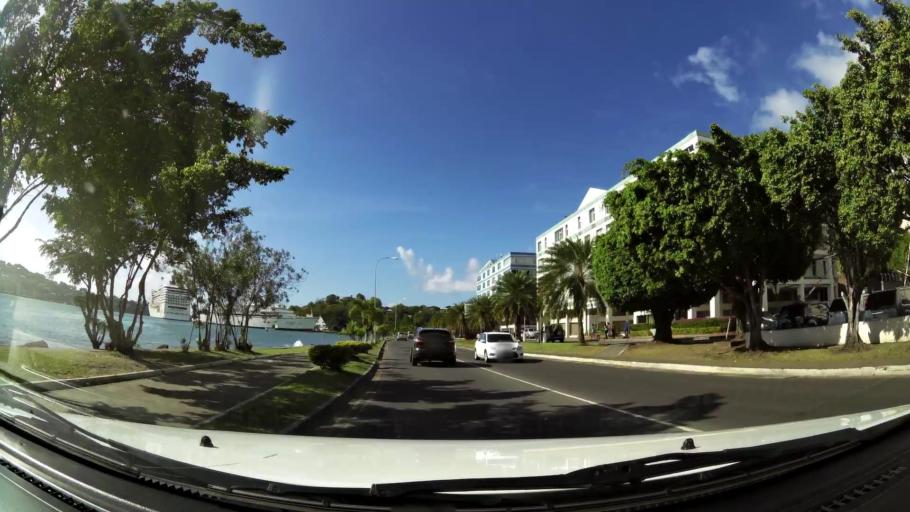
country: LC
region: Castries Quarter
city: Bisee
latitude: 14.0131
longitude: -60.9901
